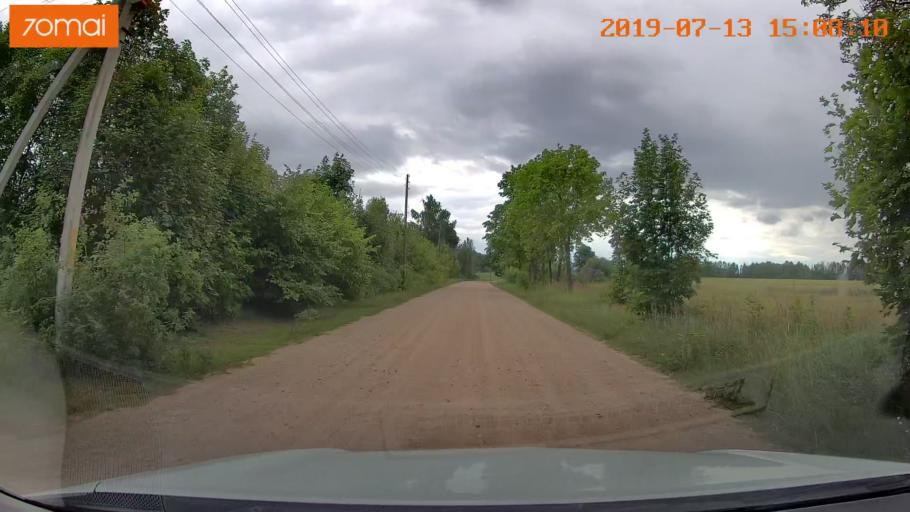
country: BY
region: Mogilev
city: Hlusha
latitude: 53.1816
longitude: 28.7574
